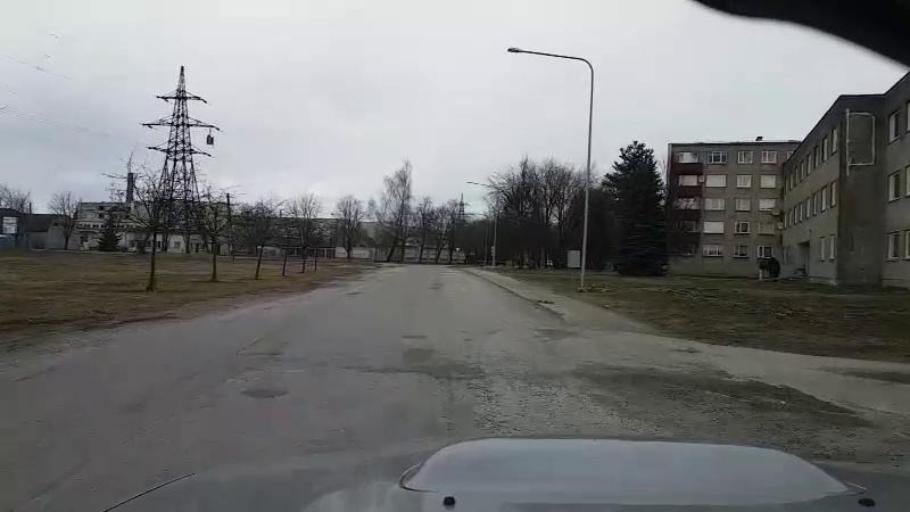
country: EE
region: Jaervamaa
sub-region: Paide linn
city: Paide
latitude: 58.8813
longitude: 25.5647
